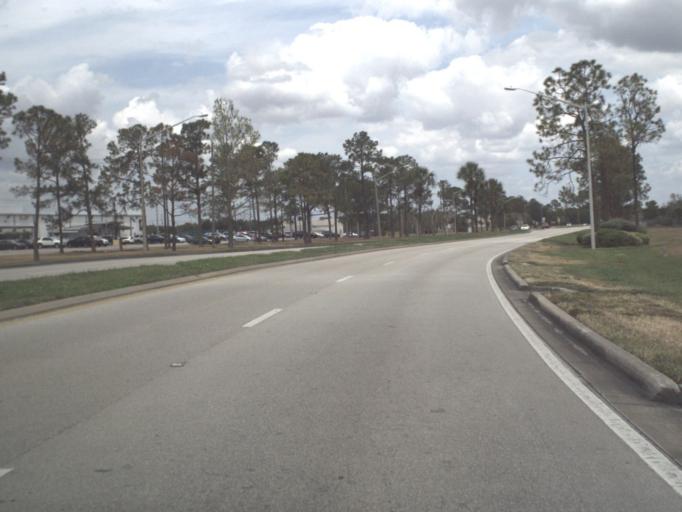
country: US
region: Florida
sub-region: Orange County
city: Taft
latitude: 28.4373
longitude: -81.3346
